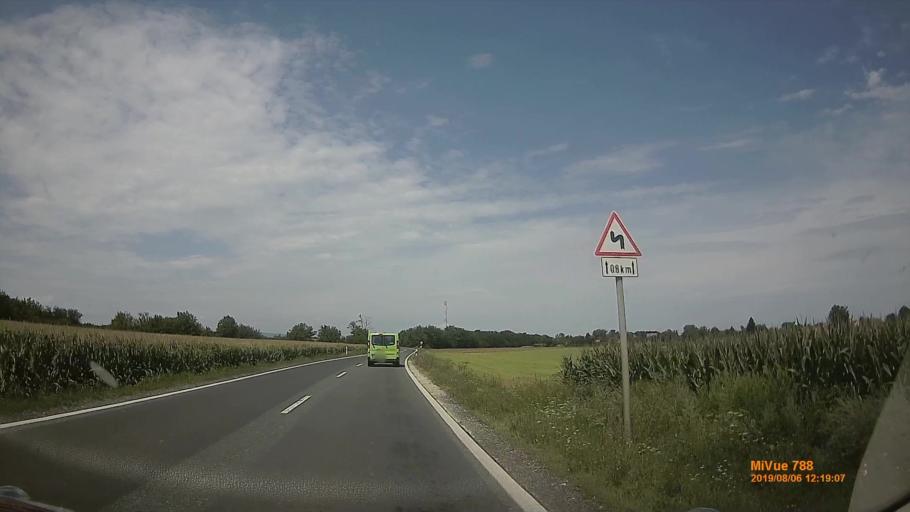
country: HU
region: Vas
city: Vep
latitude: 47.1743
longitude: 16.7657
